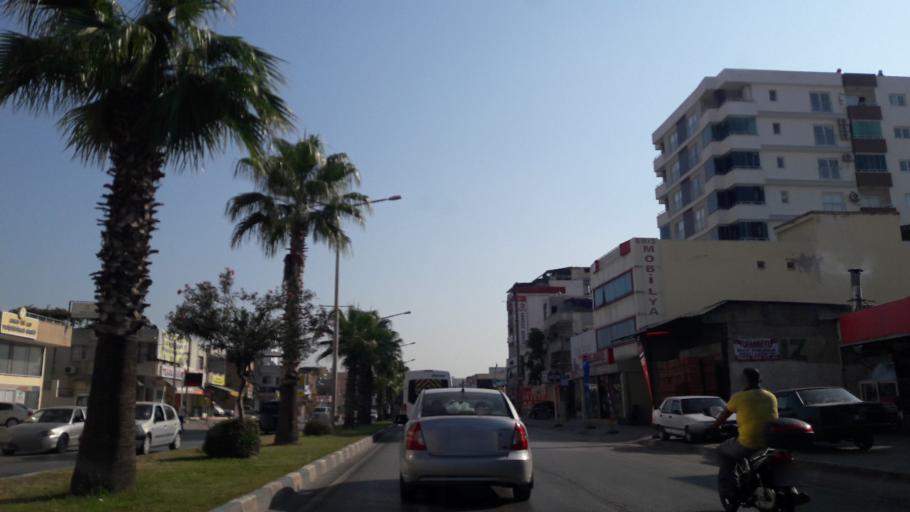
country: TR
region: Adana
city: Yuregir
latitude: 37.0330
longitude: 35.4122
